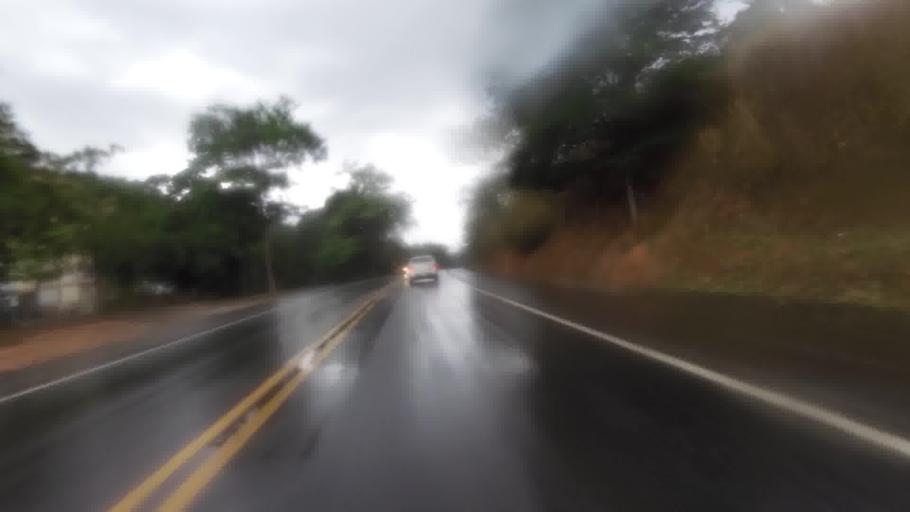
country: BR
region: Espirito Santo
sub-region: Cachoeiro De Itapemirim
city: Cachoeiro de Itapemirim
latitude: -20.9676
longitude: -41.1083
